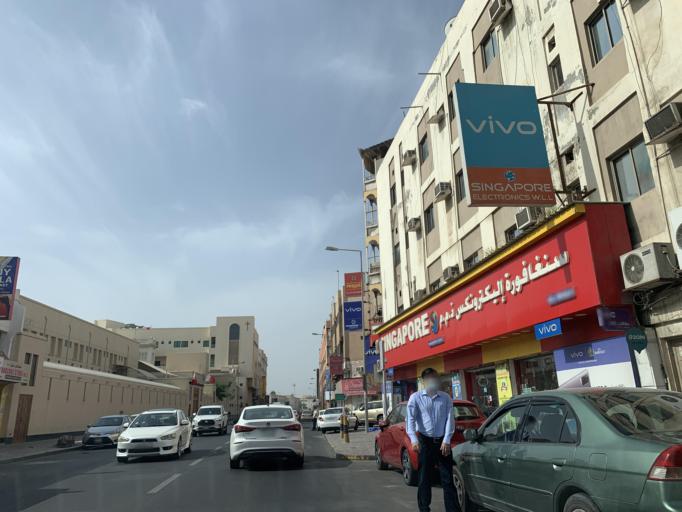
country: BH
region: Manama
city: Manama
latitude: 26.2283
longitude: 50.5799
